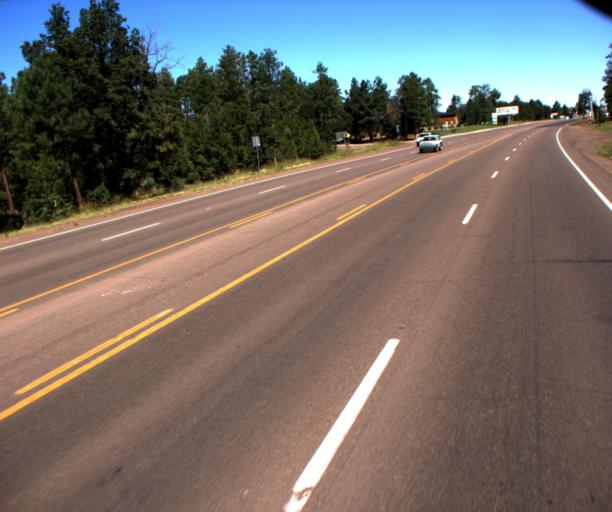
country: US
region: Arizona
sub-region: Navajo County
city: Lake of the Woods
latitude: 34.1826
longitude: -110.0143
